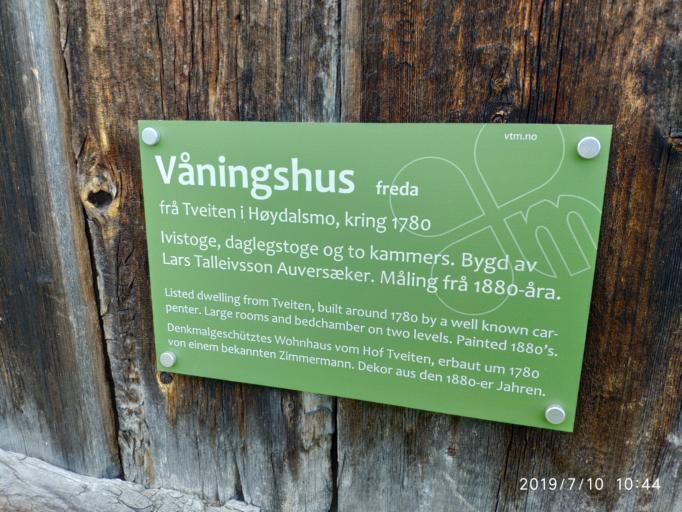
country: NO
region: Telemark
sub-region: Tokke
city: Dalen
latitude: 59.4653
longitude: 8.0212
